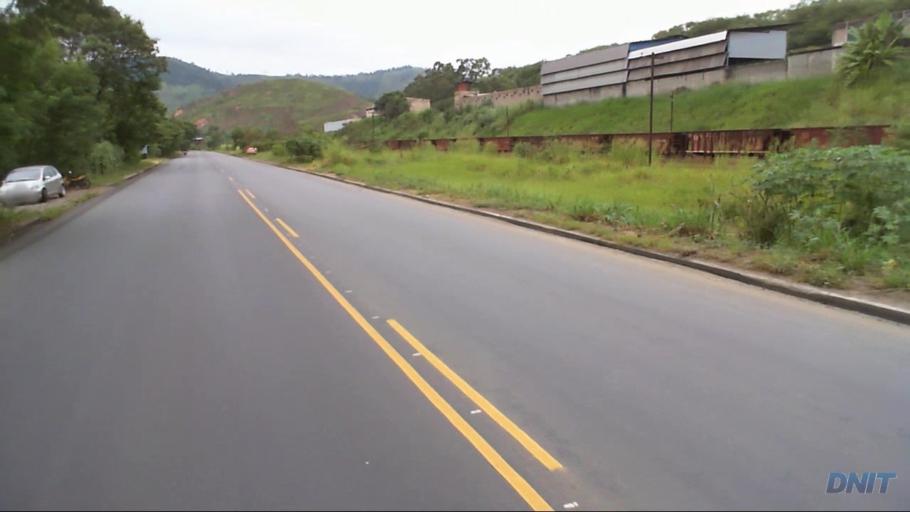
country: BR
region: Minas Gerais
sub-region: Coronel Fabriciano
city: Coronel Fabriciano
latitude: -19.5288
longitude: -42.6329
